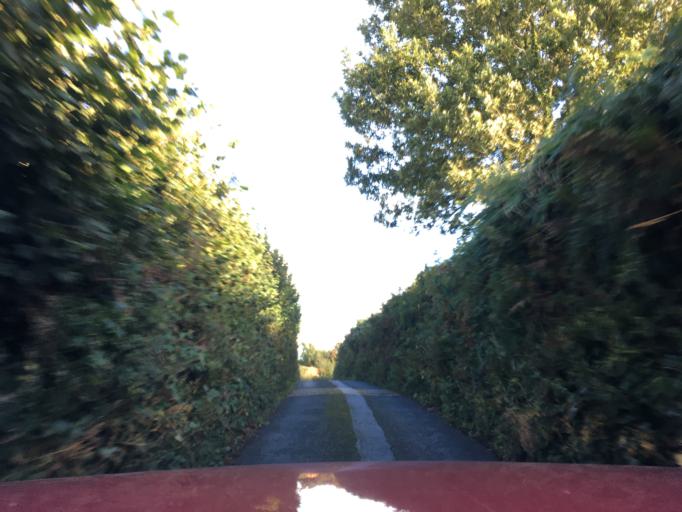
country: GB
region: England
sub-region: Devon
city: Dartmouth
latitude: 50.3317
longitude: -3.6000
